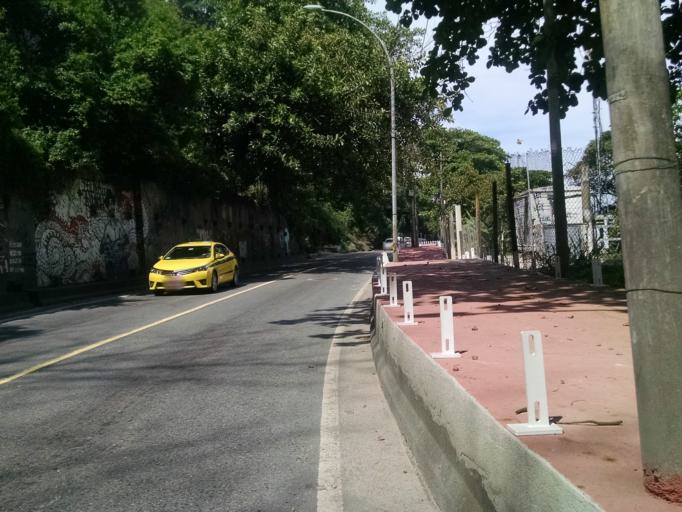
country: BR
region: Rio de Janeiro
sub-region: Rio De Janeiro
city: Rio de Janeiro
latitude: -22.9978
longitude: -43.2396
